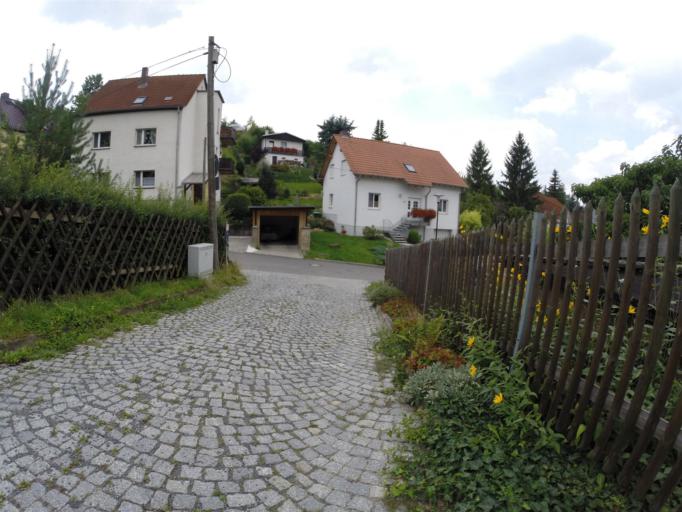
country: DE
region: Thuringia
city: Jena
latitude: 50.9300
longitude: 11.6079
